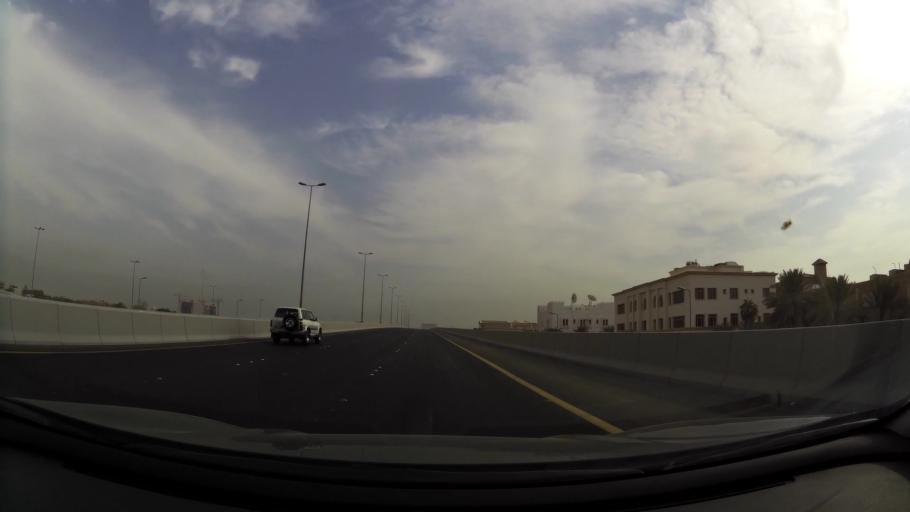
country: KW
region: Al Asimah
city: Ar Rabiyah
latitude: 29.3161
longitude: 47.8791
